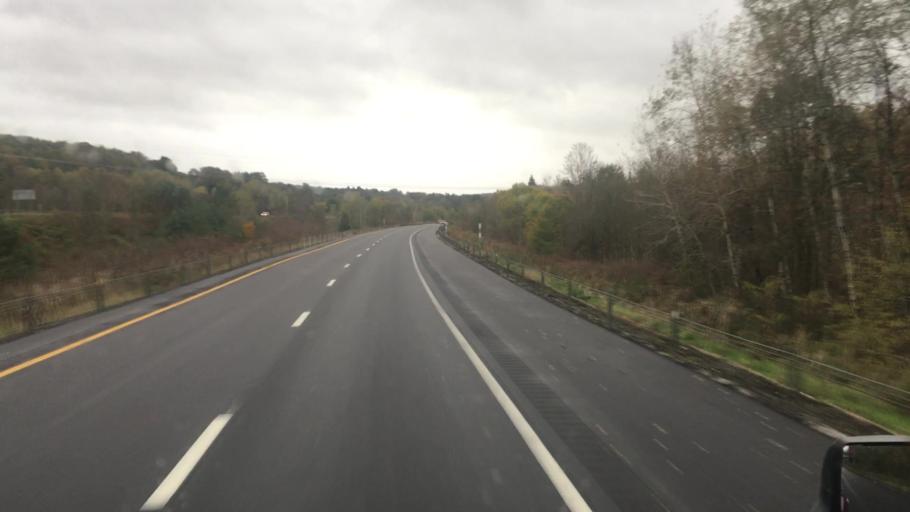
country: US
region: New York
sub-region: Chenango County
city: Bainbridge
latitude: 42.2093
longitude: -75.5186
